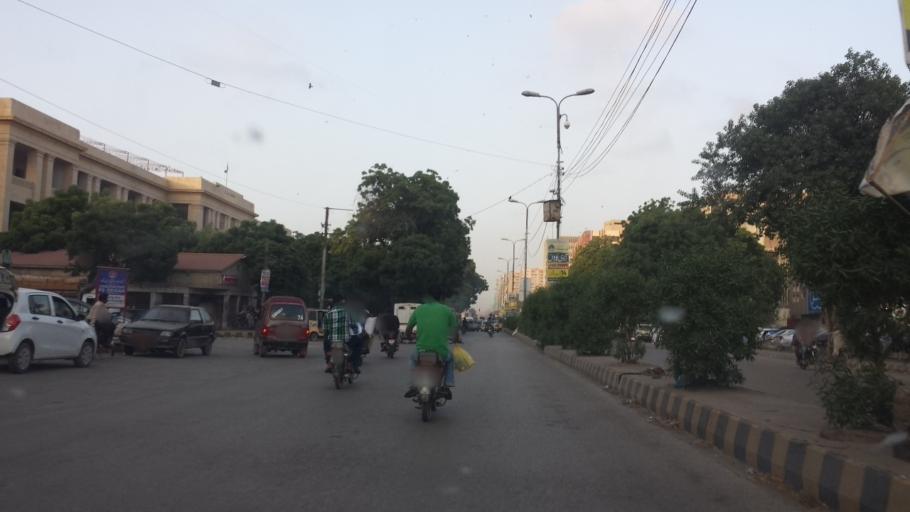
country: PK
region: Sindh
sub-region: Karachi District
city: Karachi
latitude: 24.8611
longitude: 67.0182
